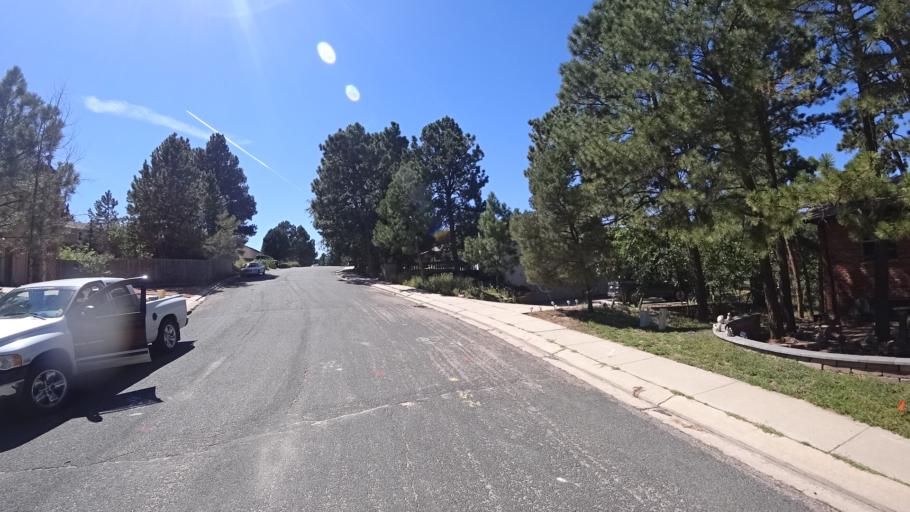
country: US
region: Colorado
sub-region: El Paso County
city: Colorado Springs
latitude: 38.9208
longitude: -104.7984
